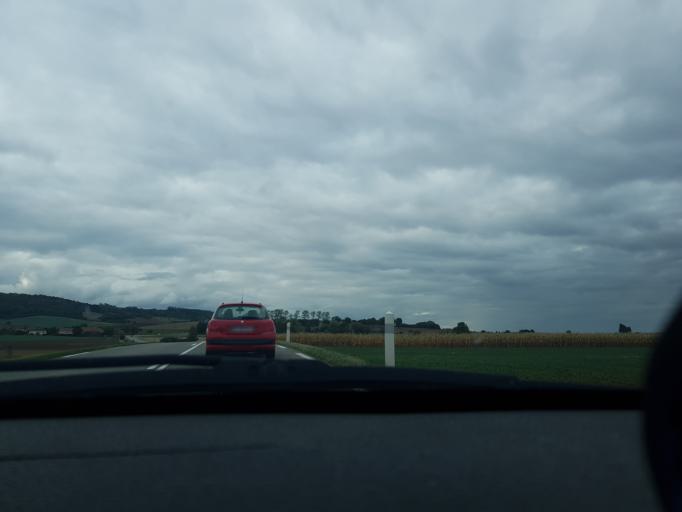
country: FR
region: Lorraine
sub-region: Departement de la Moselle
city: Chateau-Salins
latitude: 48.8336
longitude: 6.5043
